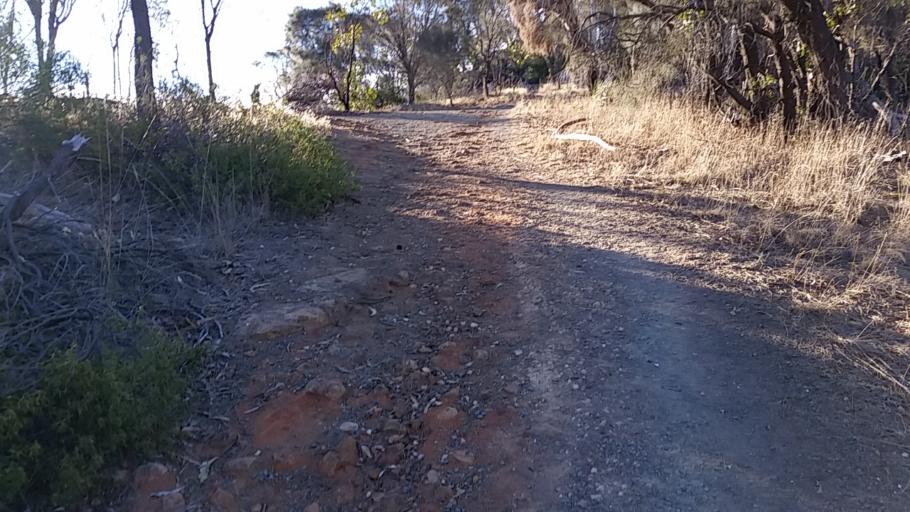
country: AU
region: South Australia
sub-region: Mount Barker
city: Nairne
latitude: -35.0655
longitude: 138.9213
